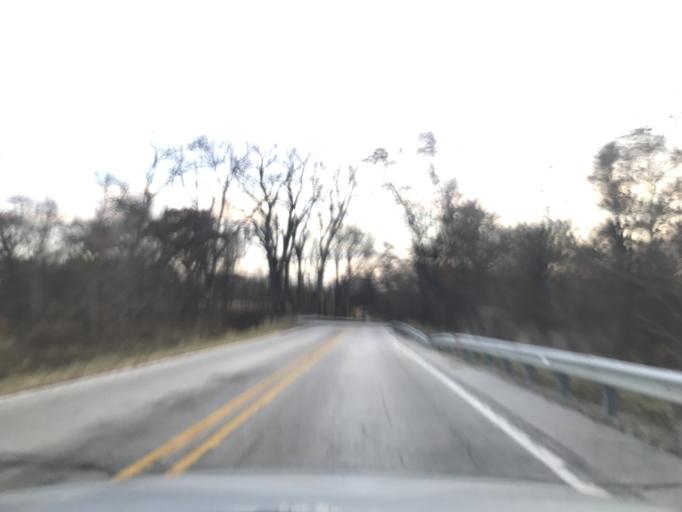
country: US
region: Illinois
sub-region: Henderson County
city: Oquawka
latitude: 40.9943
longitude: -90.8538
